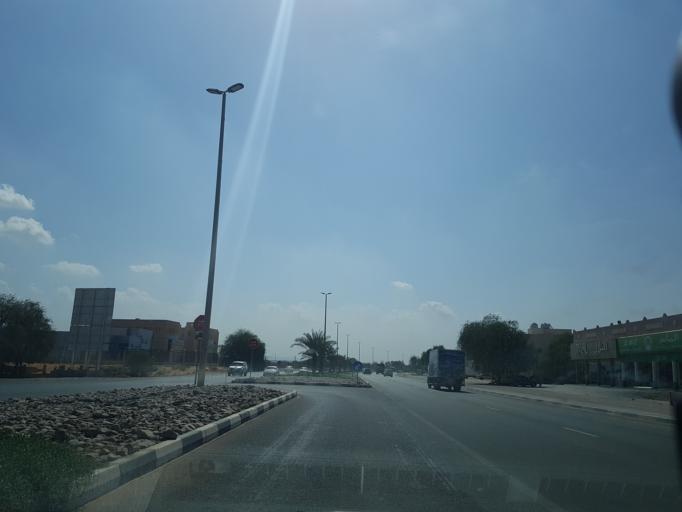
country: AE
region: Ra's al Khaymah
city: Ras al-Khaimah
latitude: 25.6951
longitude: 55.9675
